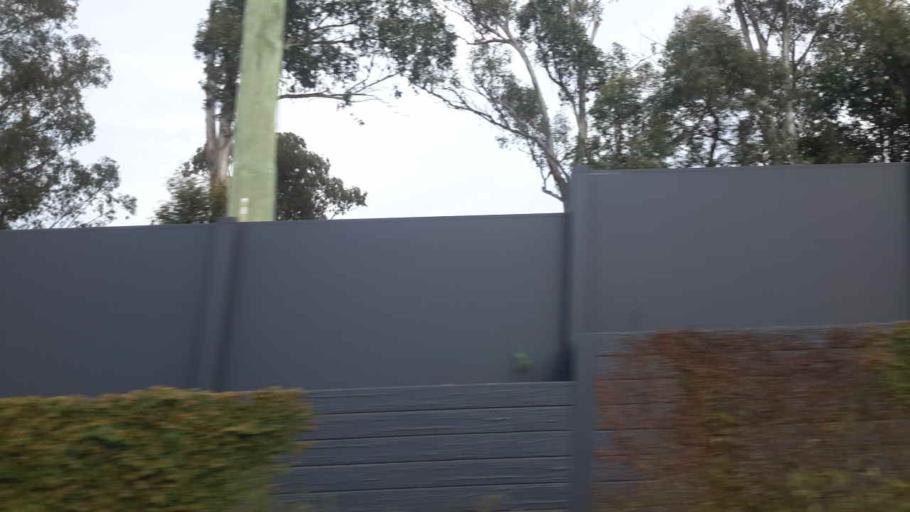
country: AU
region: New South Wales
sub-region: Penrith Municipality
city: Werrington Downs
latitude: -33.7287
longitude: 150.7197
